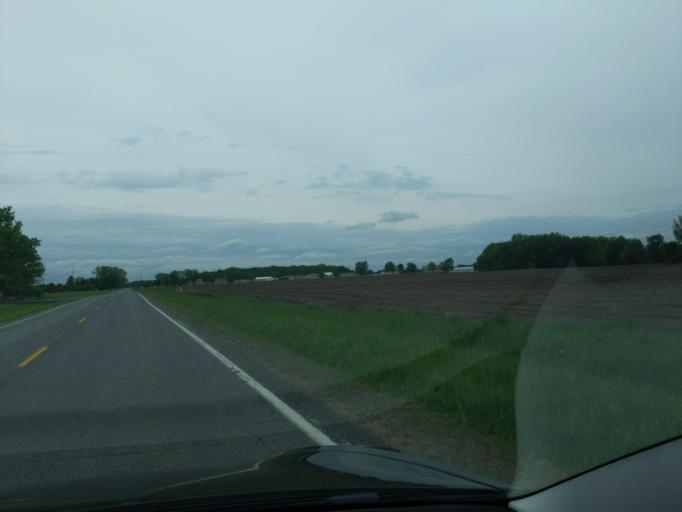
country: US
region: Michigan
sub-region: Ingham County
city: Mason
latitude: 42.5578
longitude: -84.4271
